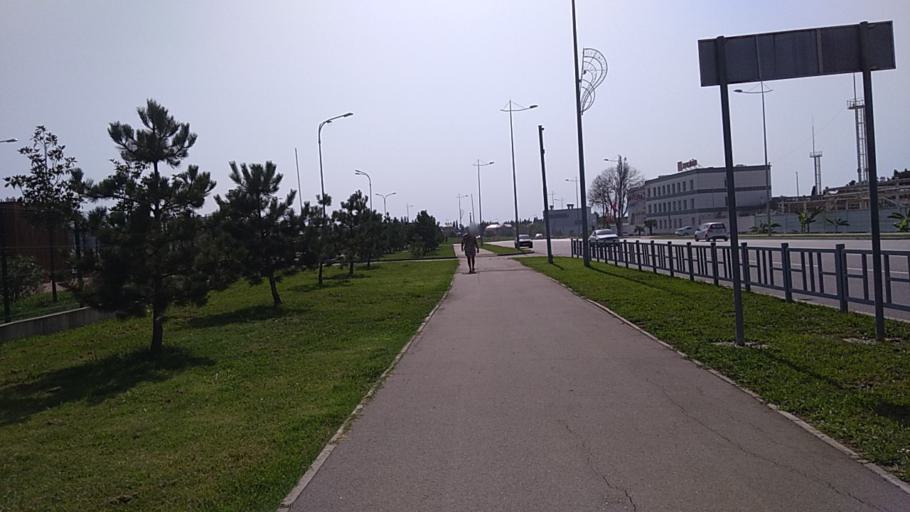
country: RU
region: Krasnodarskiy
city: Vysokoye
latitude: 43.3971
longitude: 39.9923
